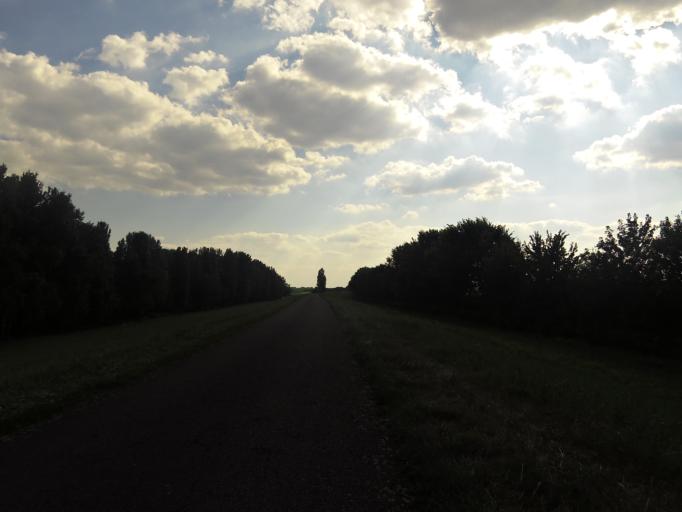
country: HU
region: Jasz-Nagykun-Szolnok
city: Abadszalok
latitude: 47.5333
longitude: 20.6195
